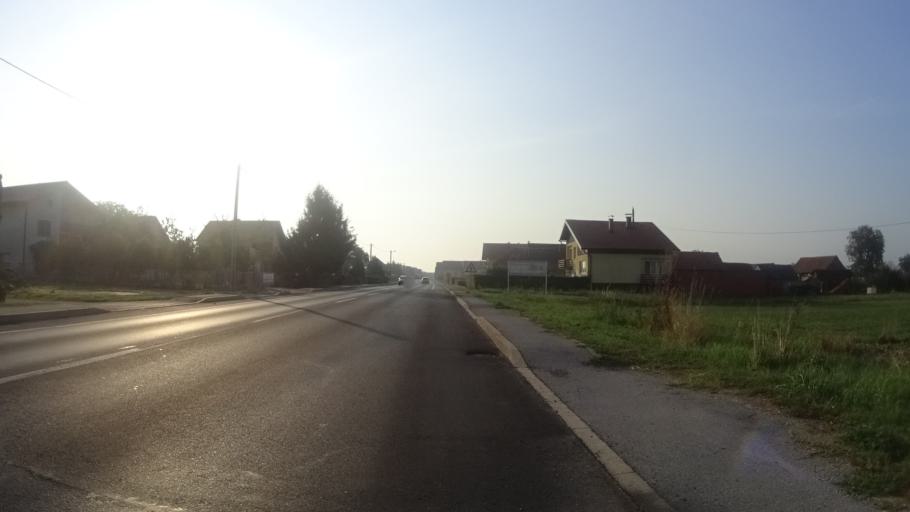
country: HR
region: Varazdinska
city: Petrijanec
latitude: 46.3427
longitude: 16.2386
